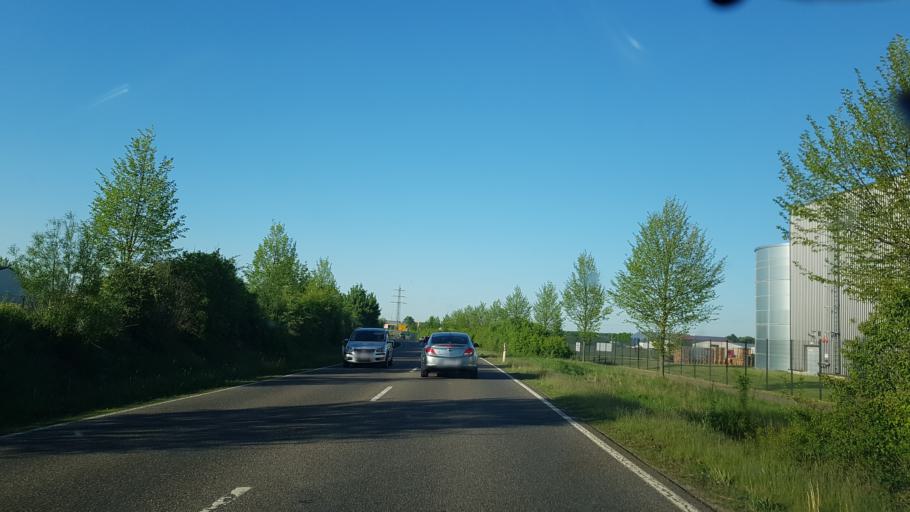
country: DE
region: North Rhine-Westphalia
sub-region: Regierungsbezirk Koln
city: Erftstadt
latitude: 50.7917
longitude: 6.7780
